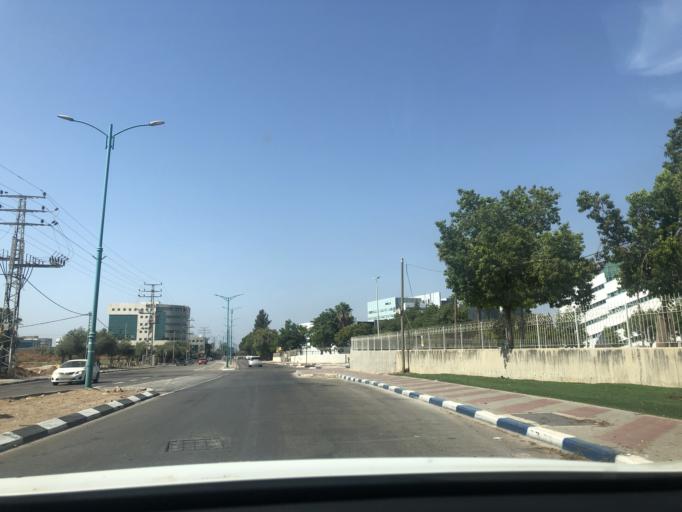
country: IL
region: Central District
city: Lod
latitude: 31.9608
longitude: 34.8990
